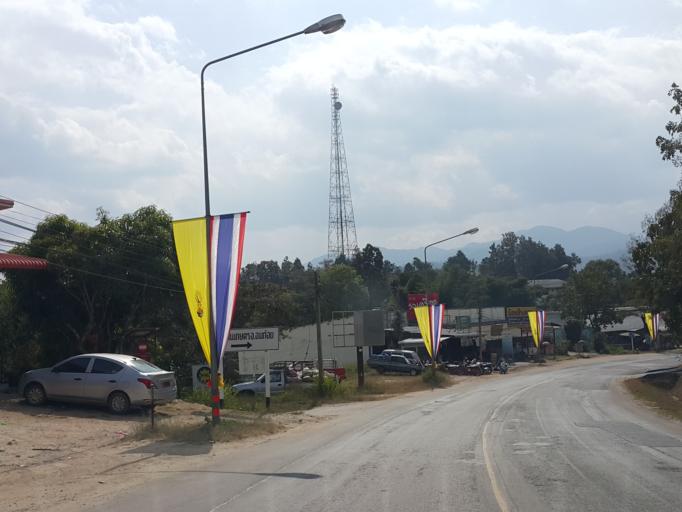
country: TH
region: Chiang Mai
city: Om Koi
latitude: 17.8029
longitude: 98.3629
